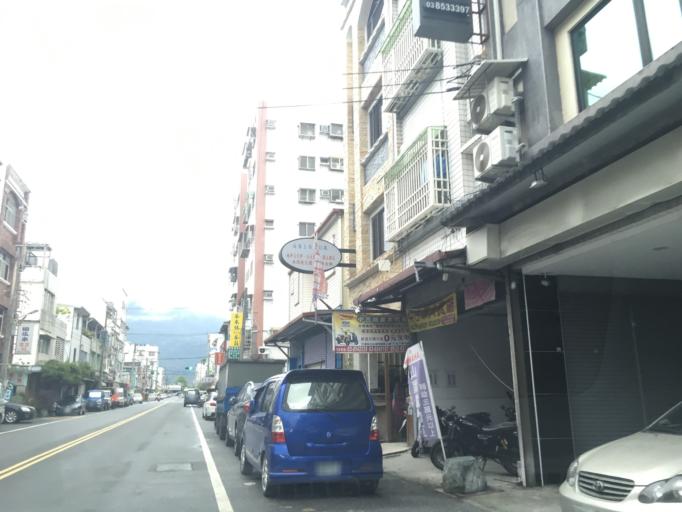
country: TW
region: Taiwan
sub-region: Hualien
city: Hualian
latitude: 23.9693
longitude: 121.5804
